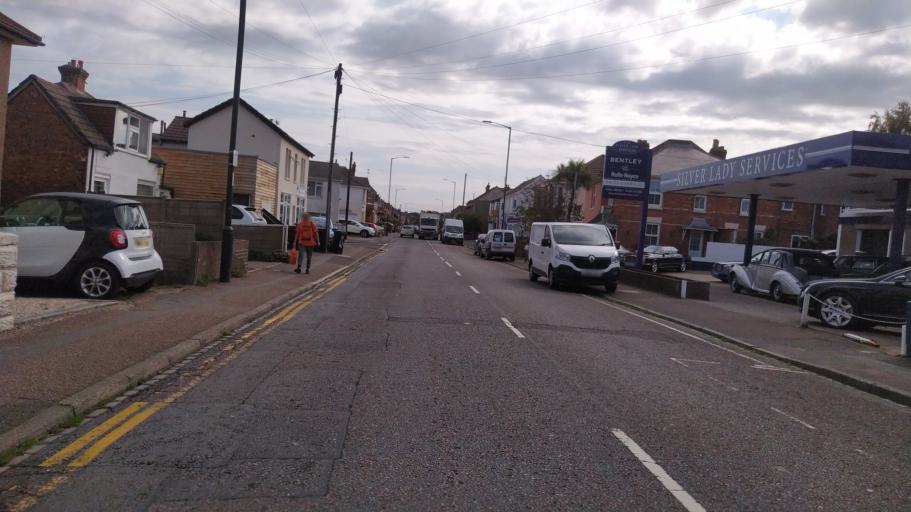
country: GB
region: England
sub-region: Bournemouth
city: Bournemouth
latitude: 50.7391
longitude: -1.8751
